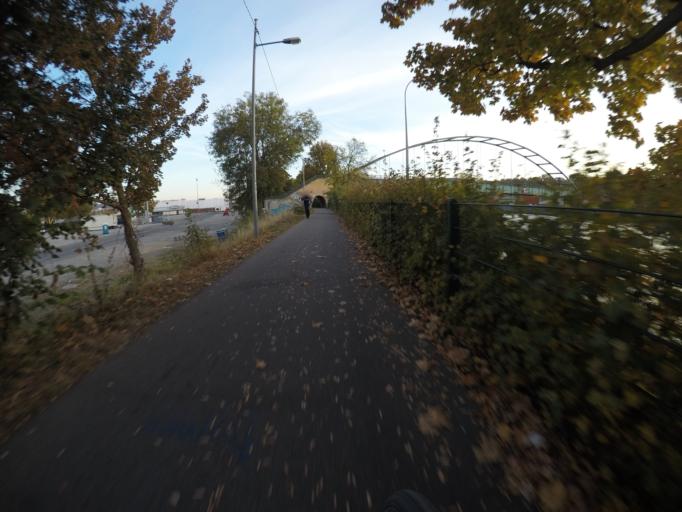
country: DE
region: Baden-Wuerttemberg
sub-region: Regierungsbezirk Stuttgart
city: Stuttgart-Ost
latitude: 48.7984
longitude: 9.2138
